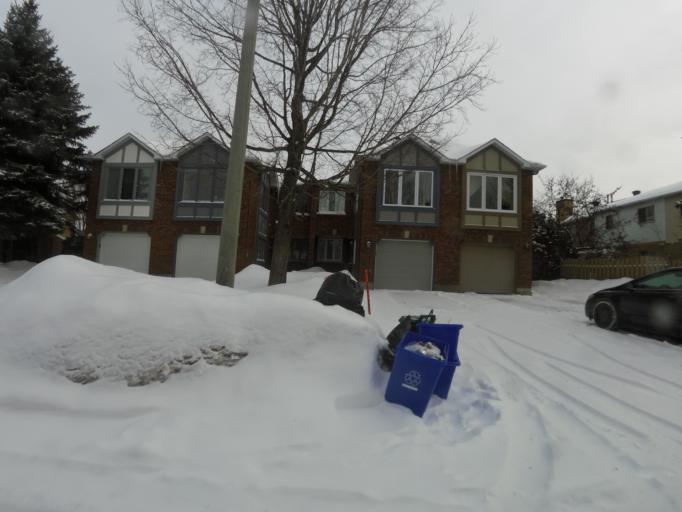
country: CA
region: Ontario
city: Ottawa
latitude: 45.3747
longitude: -75.6040
